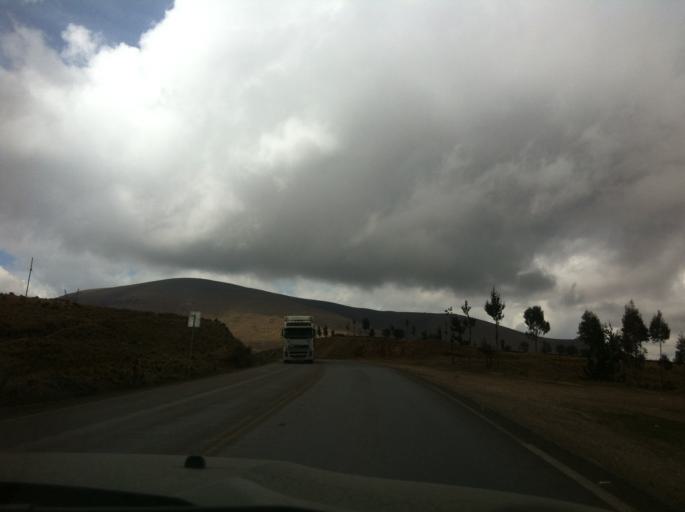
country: BO
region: Cochabamba
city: Irpa Irpa
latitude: -17.7014
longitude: -66.5243
